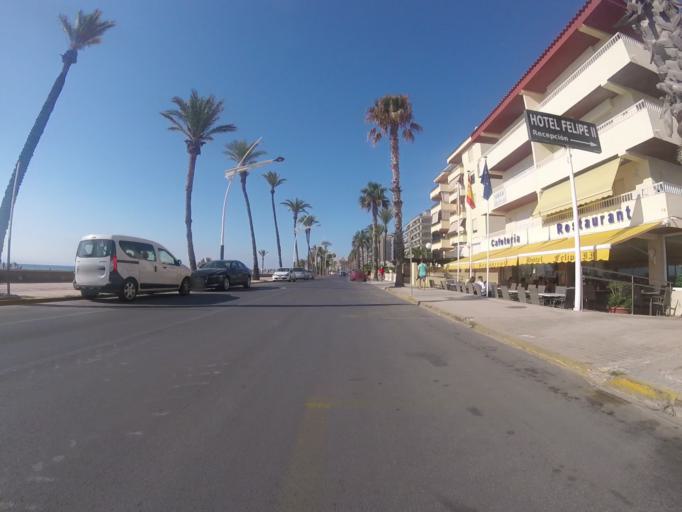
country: ES
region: Valencia
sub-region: Provincia de Castello
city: Peniscola
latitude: 40.3731
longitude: 0.4056
